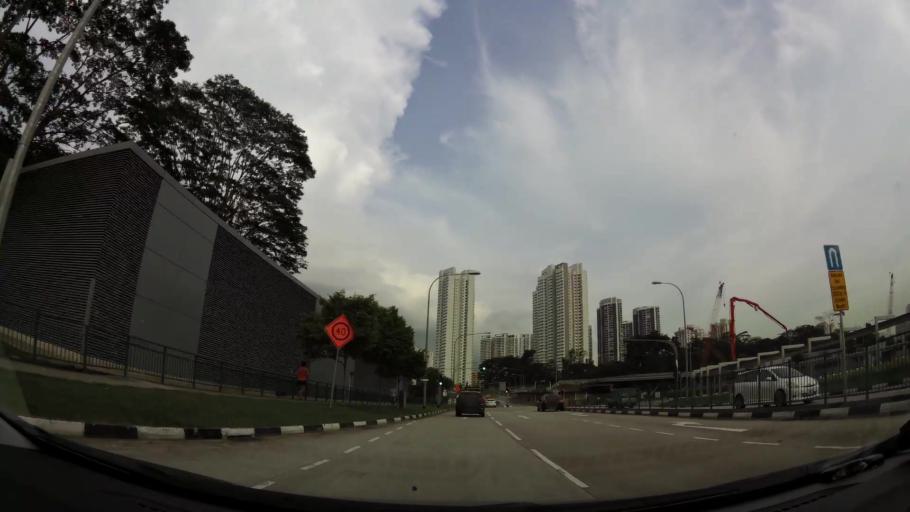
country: SG
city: Singapore
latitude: 1.3381
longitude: 103.8391
